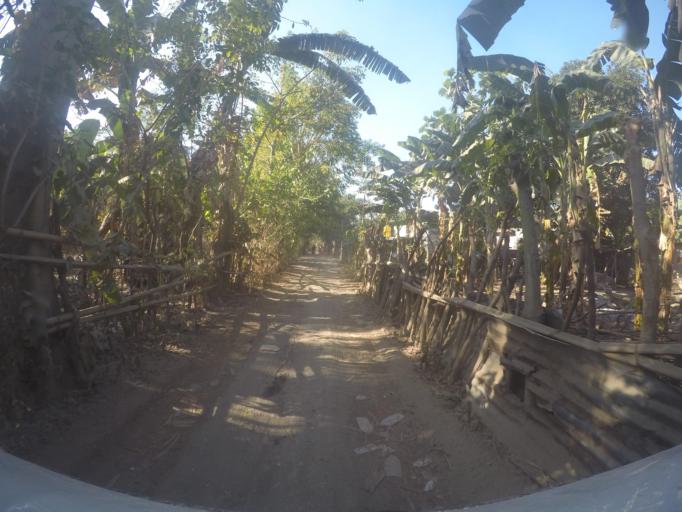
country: ID
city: Metinaro
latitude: -8.5476
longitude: 125.6665
